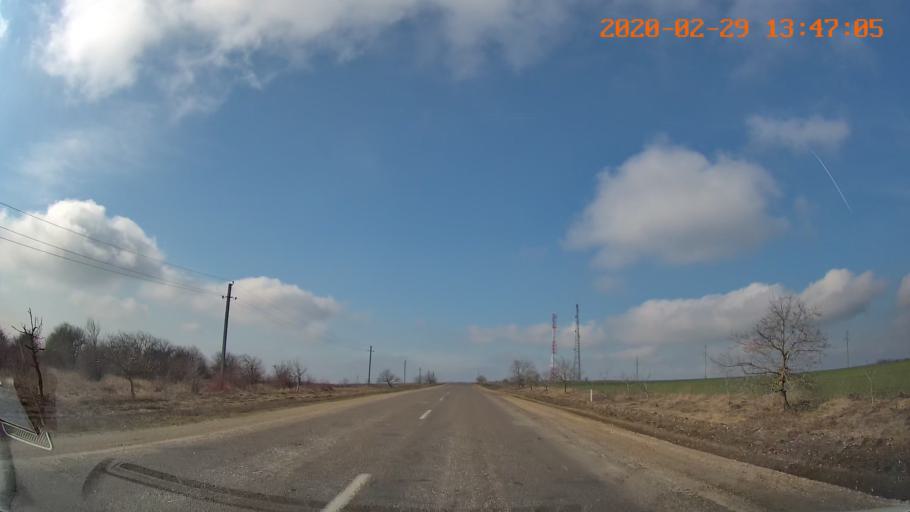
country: MD
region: Floresti
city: Leninskiy
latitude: 47.8601
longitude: 28.4939
